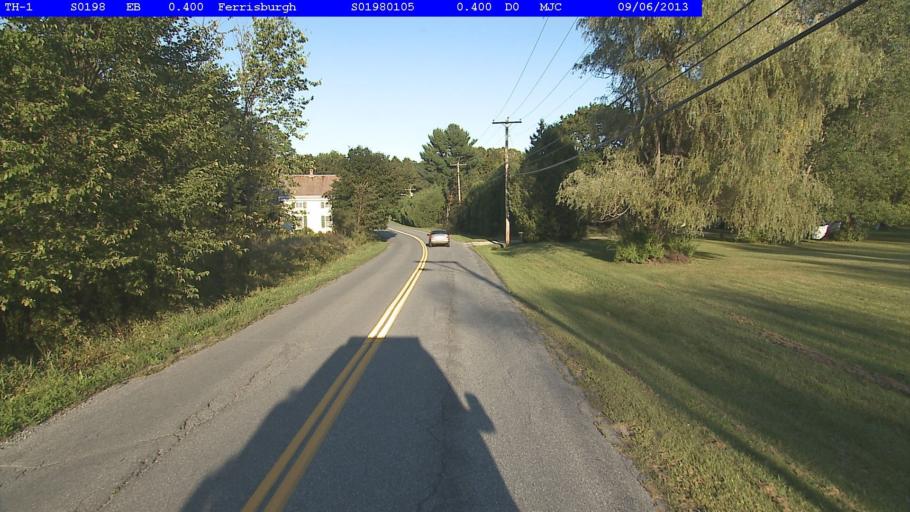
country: US
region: Vermont
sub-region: Addison County
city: Vergennes
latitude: 44.2586
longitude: -73.2201
